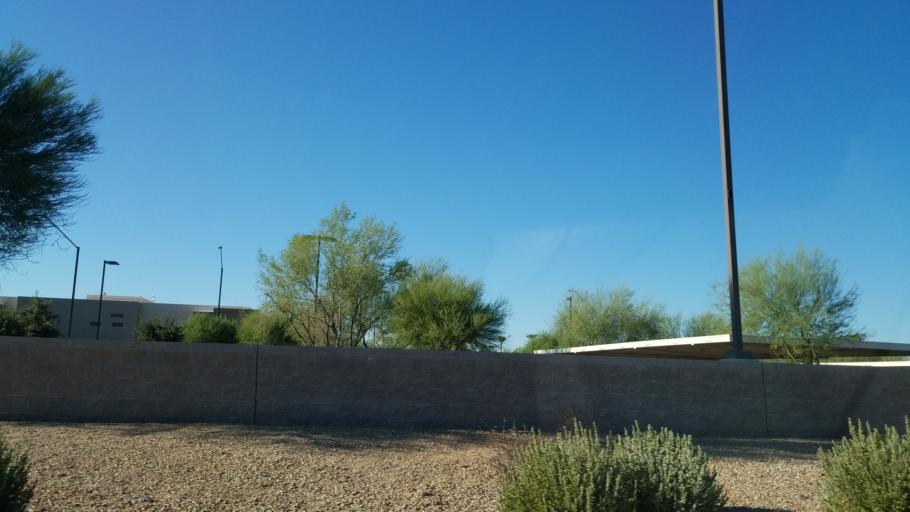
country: US
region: Arizona
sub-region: Maricopa County
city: Tolleson
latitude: 33.4458
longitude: -112.3044
